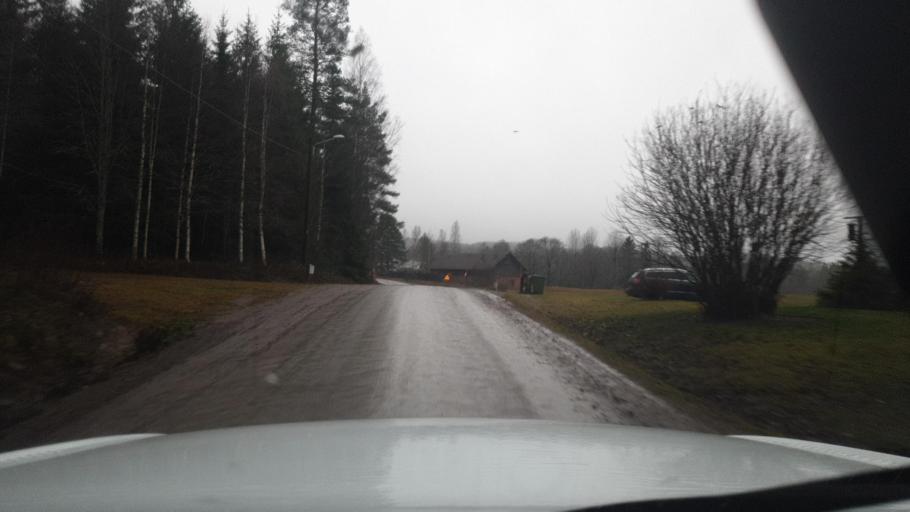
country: SE
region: Vaermland
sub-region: Arvika Kommun
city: Arvika
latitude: 59.9403
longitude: 12.6609
